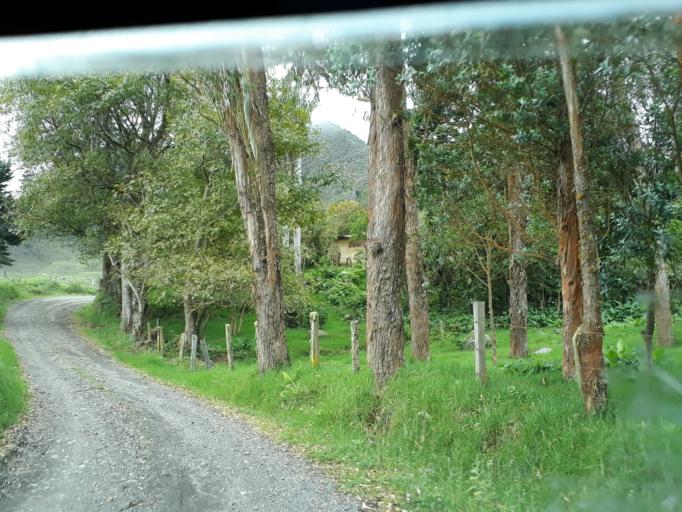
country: CO
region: Cundinamarca
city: Carmen de Carupa
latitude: 5.3770
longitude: -73.9780
